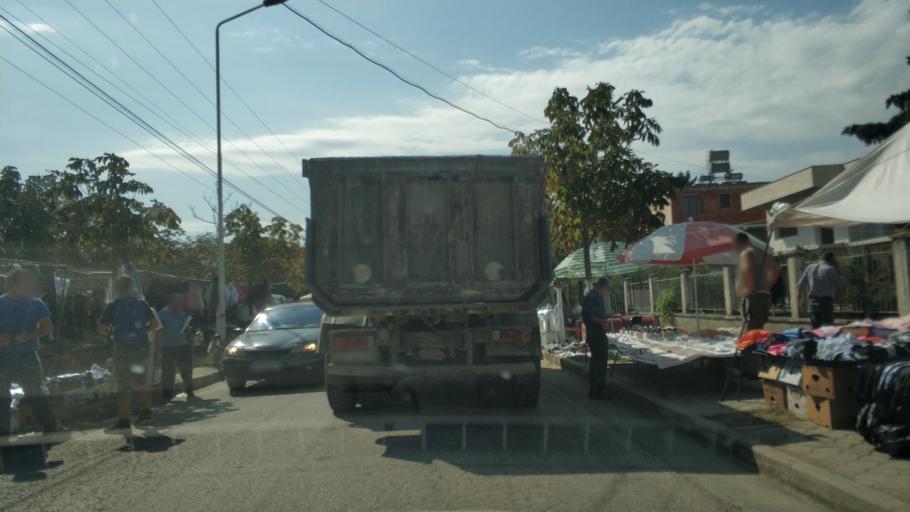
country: AL
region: Fier
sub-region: Rrethi i Lushnjes
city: Divjake
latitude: 40.9949
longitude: 19.5331
